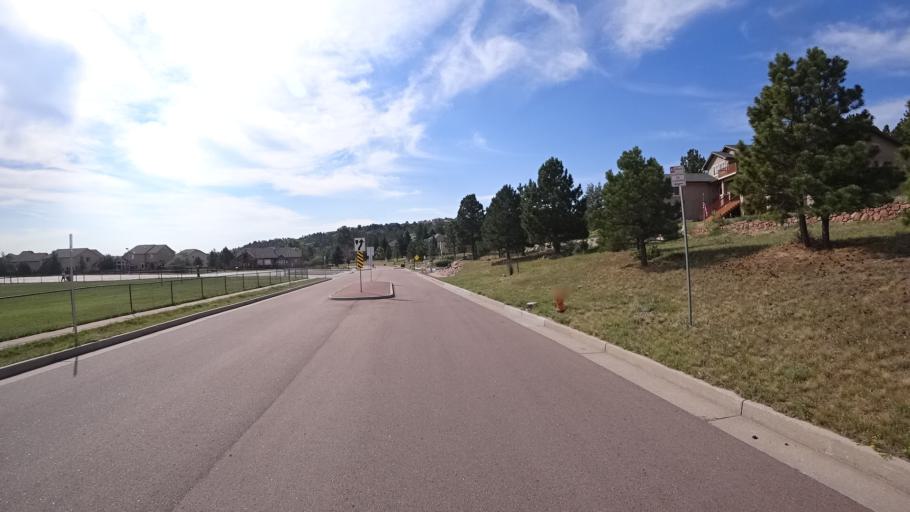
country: US
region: Colorado
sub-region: El Paso County
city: Air Force Academy
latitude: 38.9448
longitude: -104.8711
